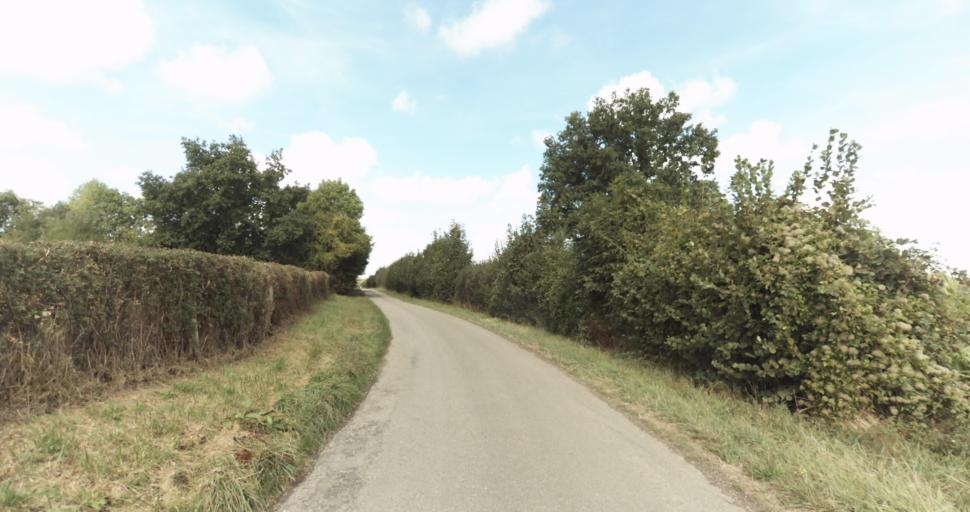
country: FR
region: Lower Normandy
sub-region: Departement du Calvados
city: Orbec
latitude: 48.9700
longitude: 0.3794
